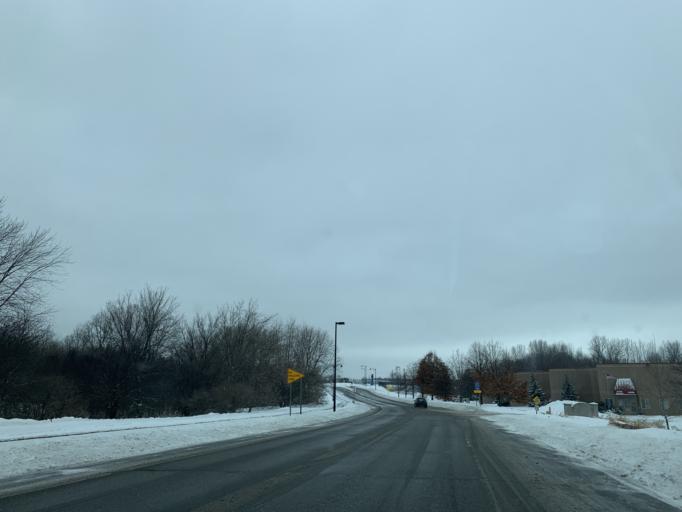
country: US
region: Minnesota
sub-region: Ramsey County
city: North Saint Paul
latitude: 45.0239
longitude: -92.9690
